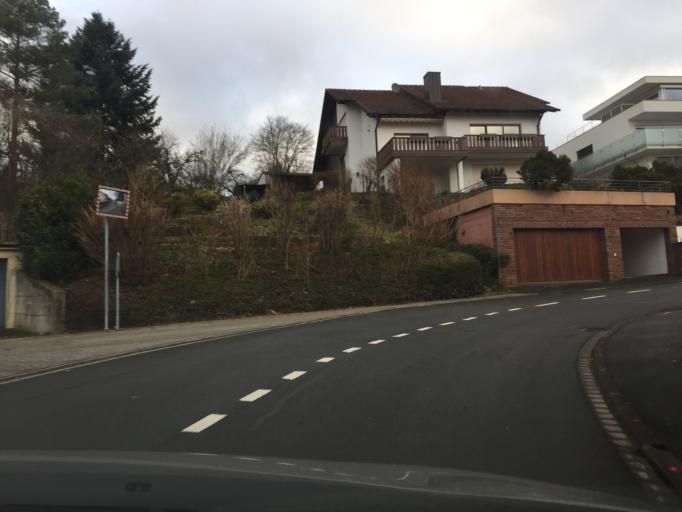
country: DE
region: Bavaria
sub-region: Regierungsbezirk Unterfranken
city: Goldbach
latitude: 49.9990
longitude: 9.1712
